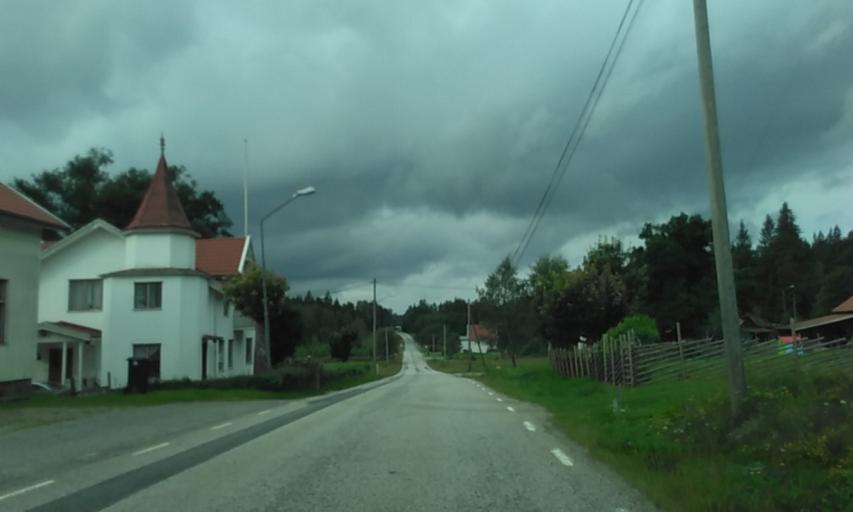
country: SE
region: Vaestra Goetaland
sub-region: Bollebygds Kommun
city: Bollebygd
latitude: 57.7527
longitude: 12.6168
